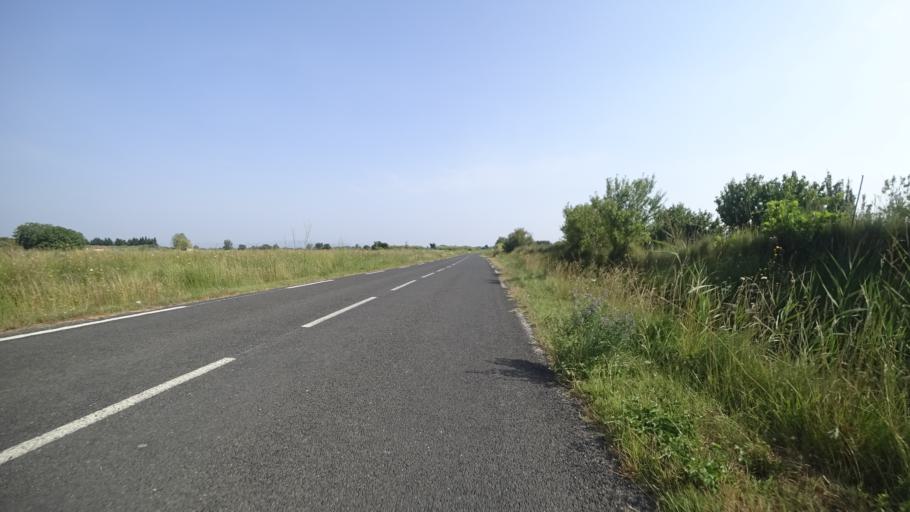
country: FR
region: Languedoc-Roussillon
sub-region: Departement des Pyrenees-Orientales
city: Villelongue-de-la-Salanque
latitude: 42.7349
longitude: 2.9892
